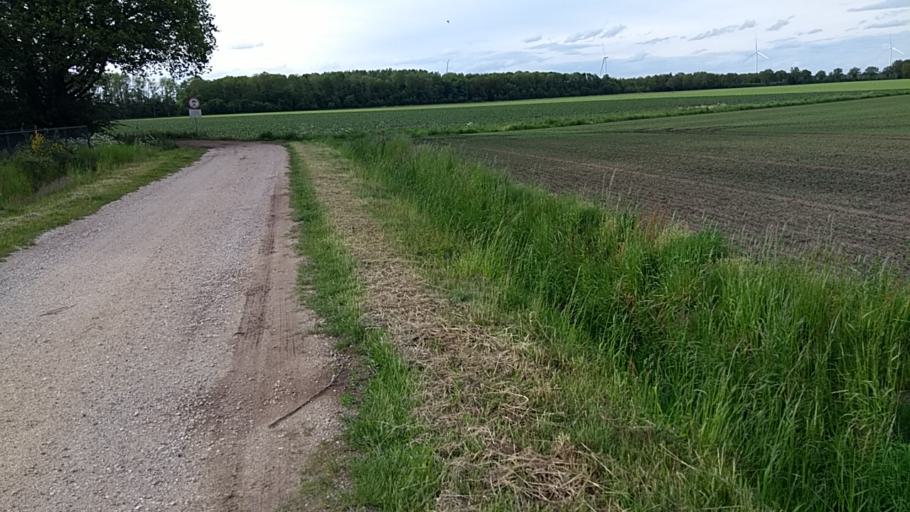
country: NL
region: Limburg
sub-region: Gemeente Leudal
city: Heythuysen
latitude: 51.2849
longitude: 5.8445
